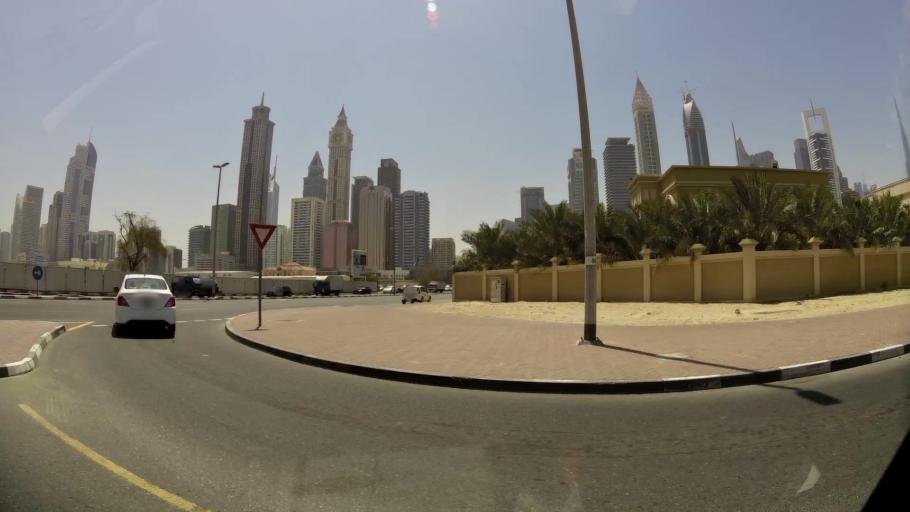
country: AE
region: Dubai
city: Dubai
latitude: 25.2174
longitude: 55.2723
